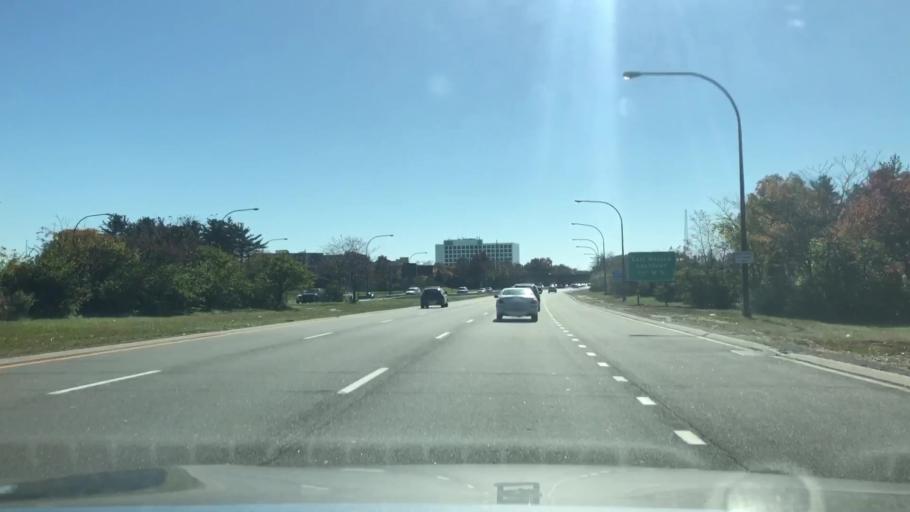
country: US
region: New York
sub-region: Nassau County
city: East Garden City
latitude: 40.7256
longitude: -73.5807
